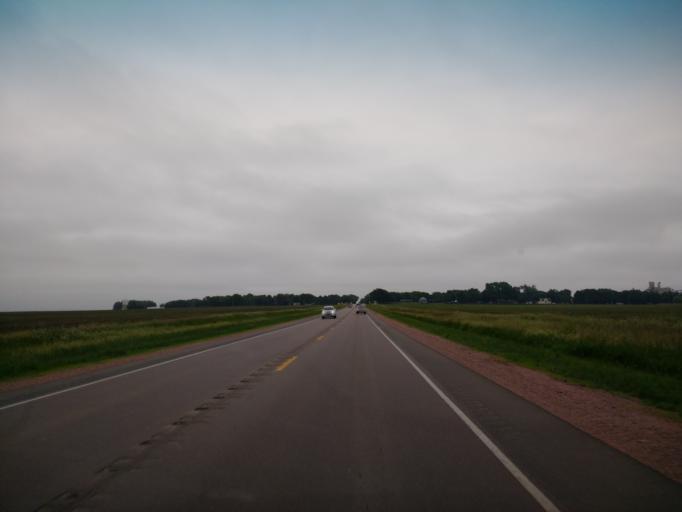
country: US
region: Iowa
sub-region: O'Brien County
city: Sanborn
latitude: 43.1860
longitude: -95.6723
